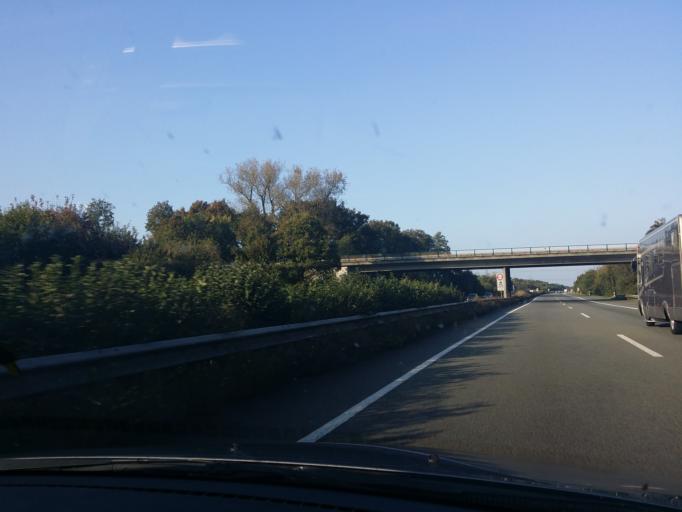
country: DE
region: Lower Saxony
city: Rieste
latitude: 52.4431
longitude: 8.0367
